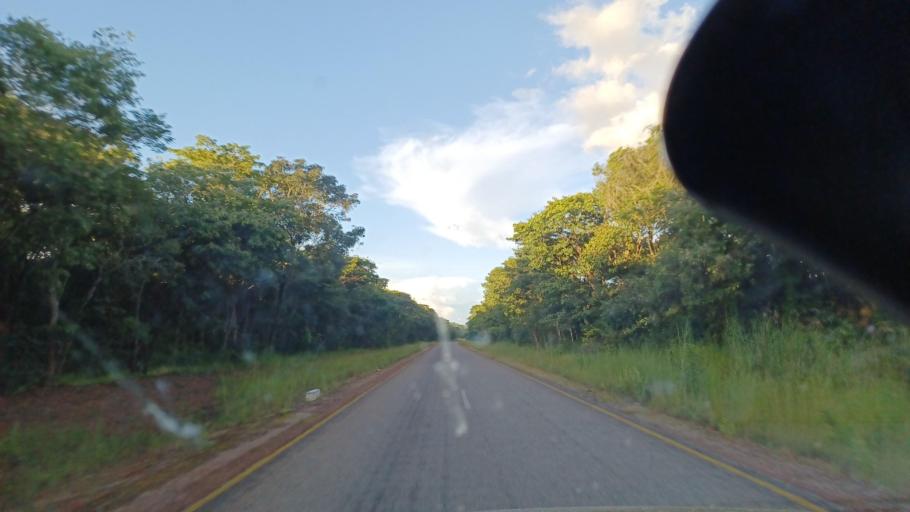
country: ZM
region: North-Western
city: Kalengwa
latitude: -13.1099
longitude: 25.2197
